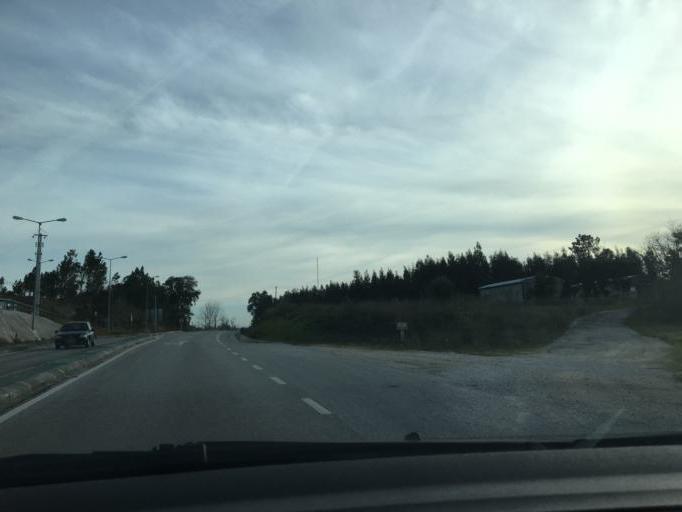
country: PT
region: Coimbra
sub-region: Soure
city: Alfarelos
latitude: 40.1997
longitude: -8.6437
